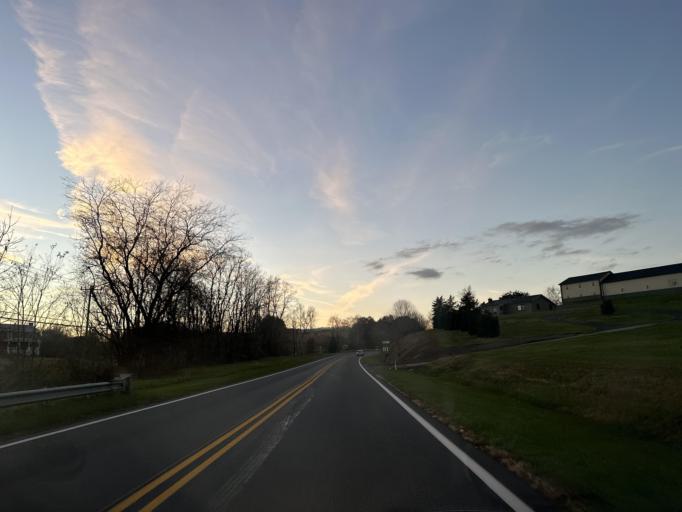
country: US
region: Virginia
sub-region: Rockingham County
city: Bridgewater
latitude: 38.4210
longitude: -79.0116
